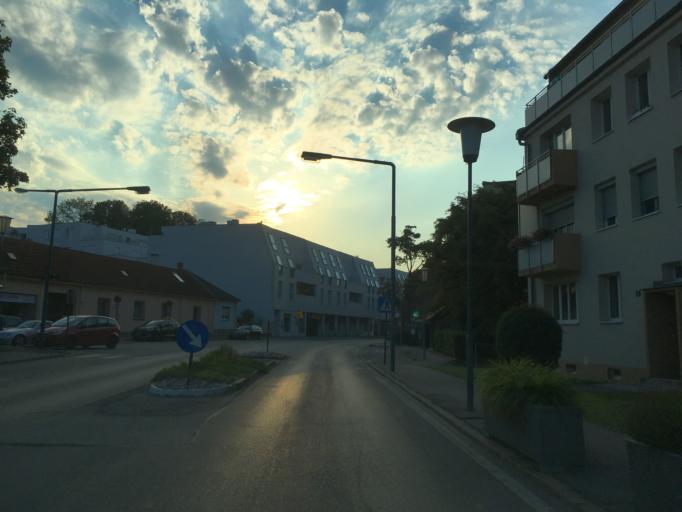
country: AT
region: Lower Austria
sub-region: Politischer Bezirk Baden
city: Bad Voslau
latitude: 47.9637
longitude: 16.2164
